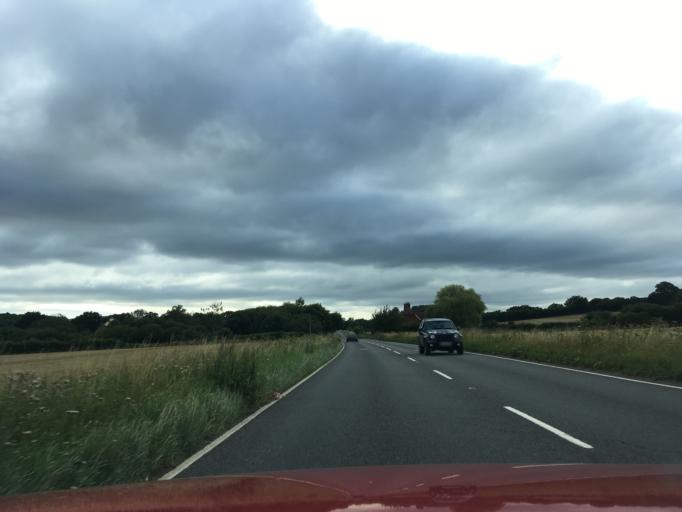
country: GB
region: England
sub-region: Hampshire
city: Liss
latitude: 51.0066
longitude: -0.8729
